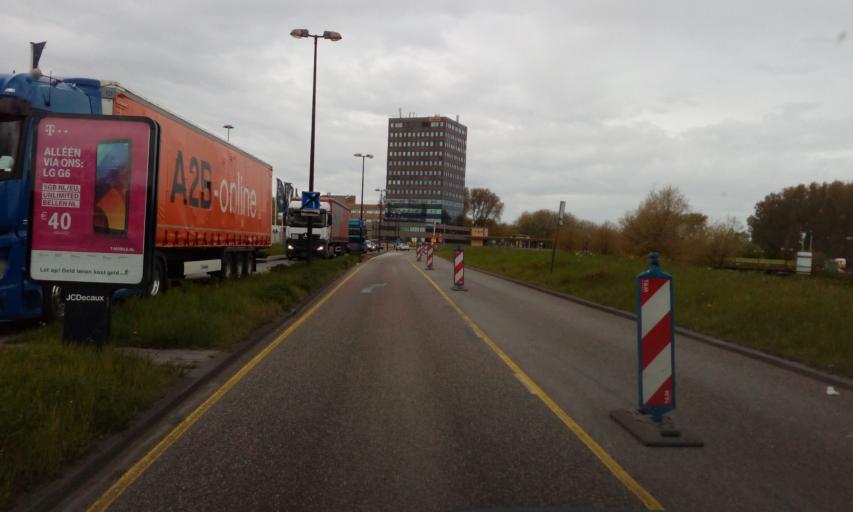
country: NL
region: South Holland
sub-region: Gemeente Vlaardingen
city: Vlaardingen
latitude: 51.9093
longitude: 4.3645
